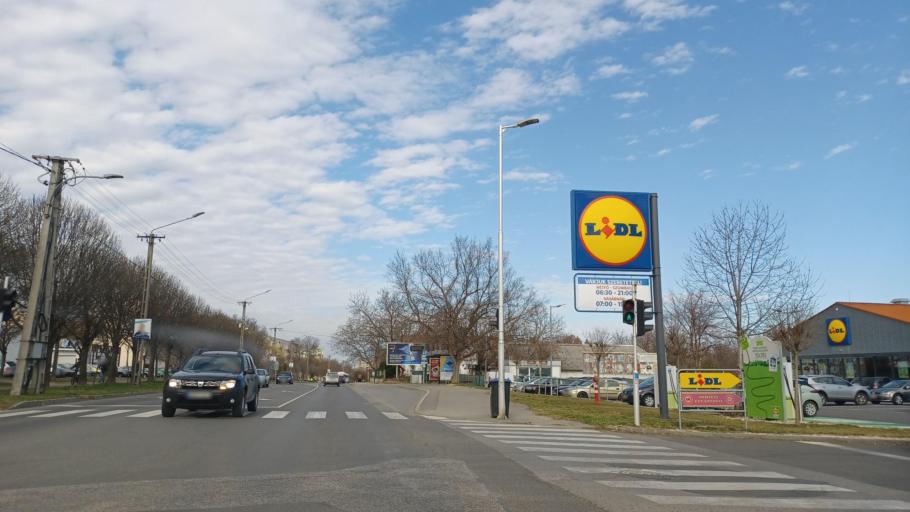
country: HU
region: Tolna
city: Szekszard
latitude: 46.3341
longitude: 18.7003
